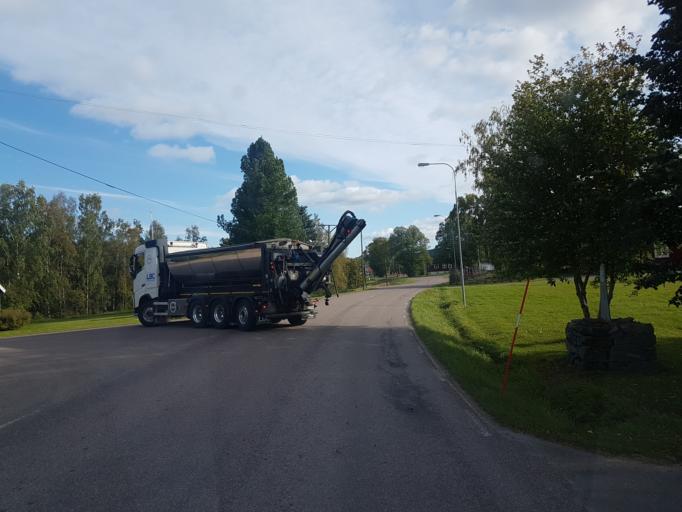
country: SE
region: Dalarna
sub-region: Saters Kommun
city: Saeter
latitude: 60.4011
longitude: 15.6371
